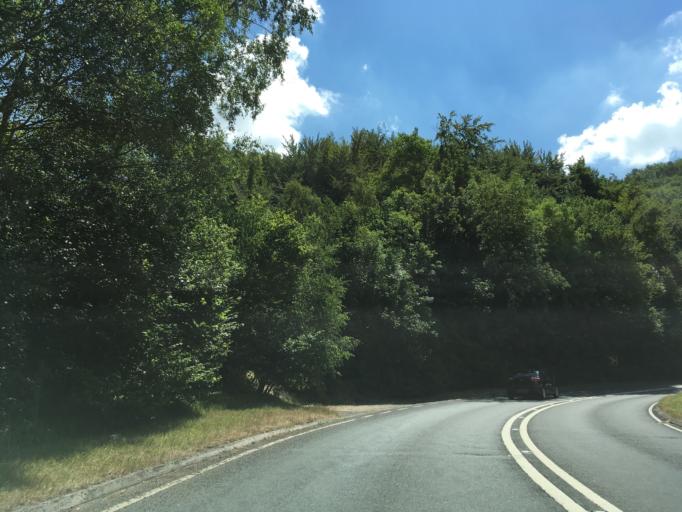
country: GB
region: England
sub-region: Gloucestershire
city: Painswick
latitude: 51.8261
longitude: -2.1660
